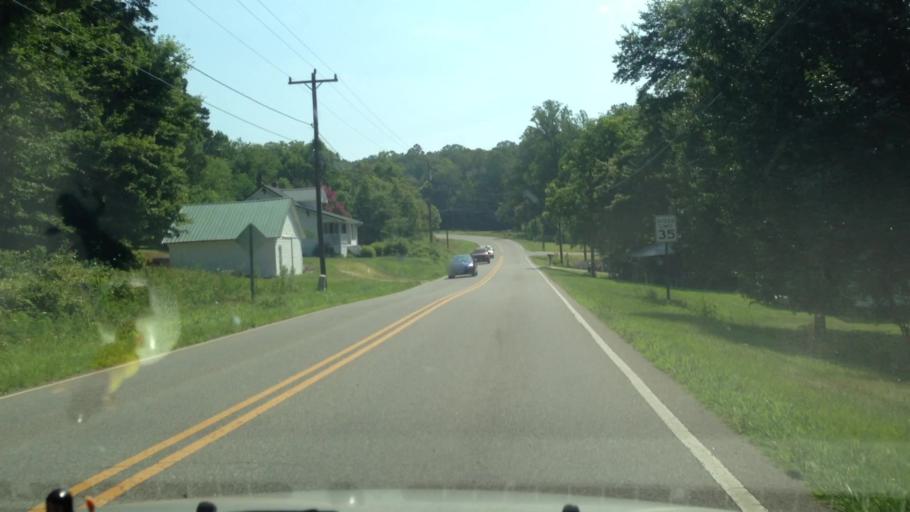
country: US
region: North Carolina
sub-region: Surry County
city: Flat Rock
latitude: 36.5141
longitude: -80.5618
